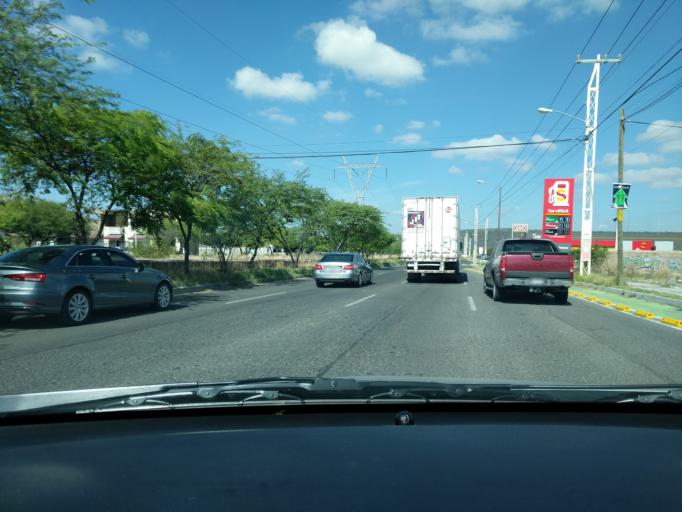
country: MX
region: Queretaro
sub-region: Queretaro
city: Patria Nueva
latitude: 20.6450
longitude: -100.4851
